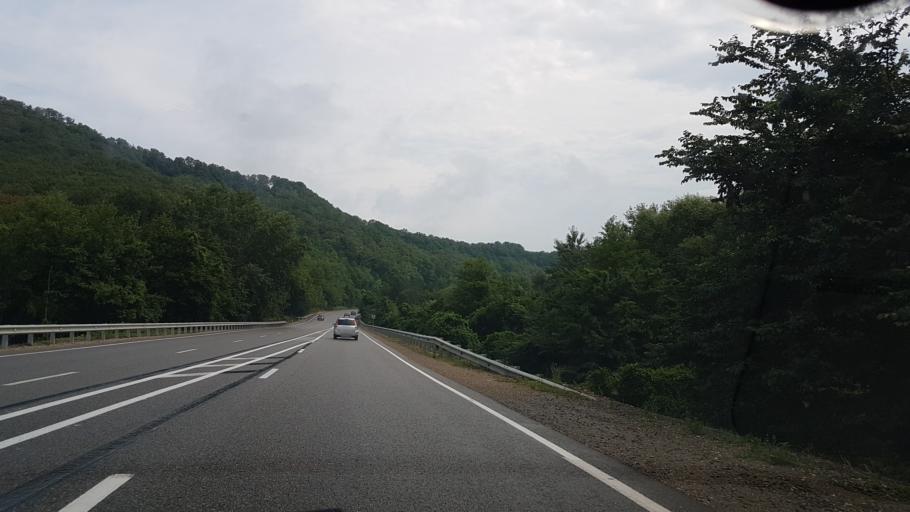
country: RU
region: Krasnodarskiy
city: Lermontovo
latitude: 44.4465
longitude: 38.7881
